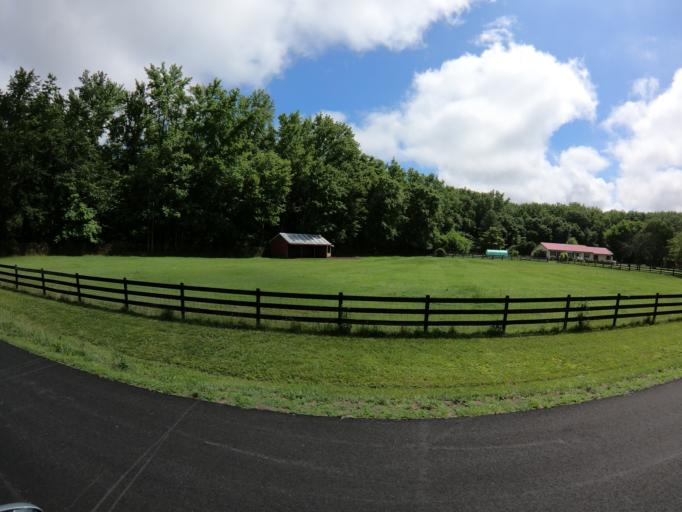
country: US
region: Maryland
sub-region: Caroline County
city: Greensboro
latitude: 39.0436
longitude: -75.8058
